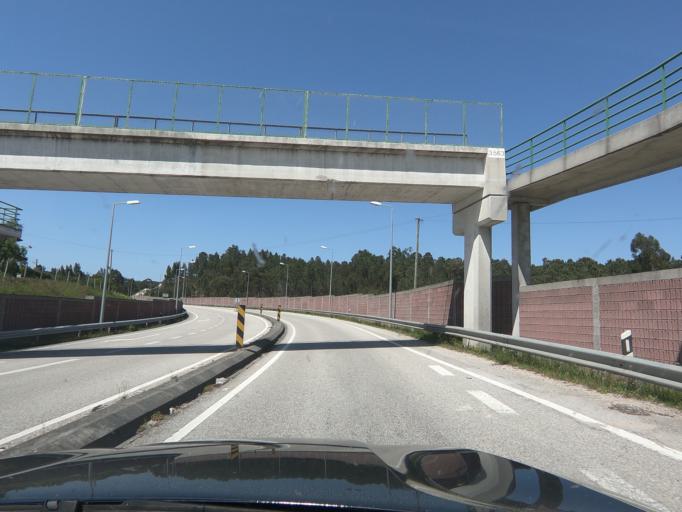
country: PT
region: Coimbra
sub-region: Miranda do Corvo
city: Miranda do Corvo
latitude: 40.0916
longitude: -8.3157
